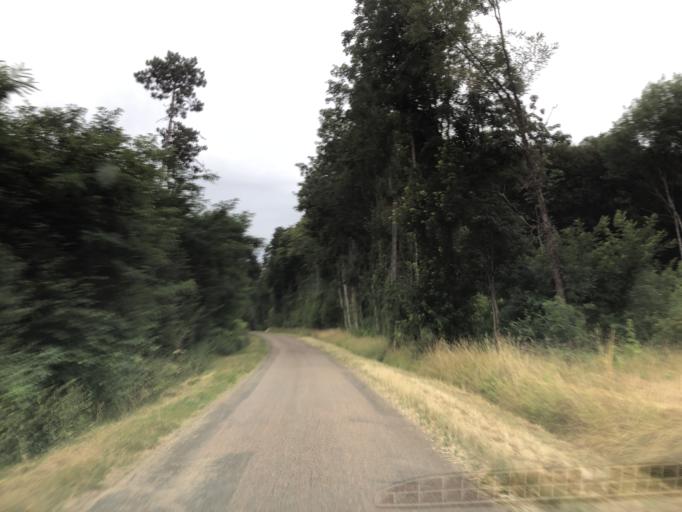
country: FR
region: Bourgogne
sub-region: Departement de l'Yonne
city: Aillant-sur-Tholon
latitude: 47.9025
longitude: 3.3183
